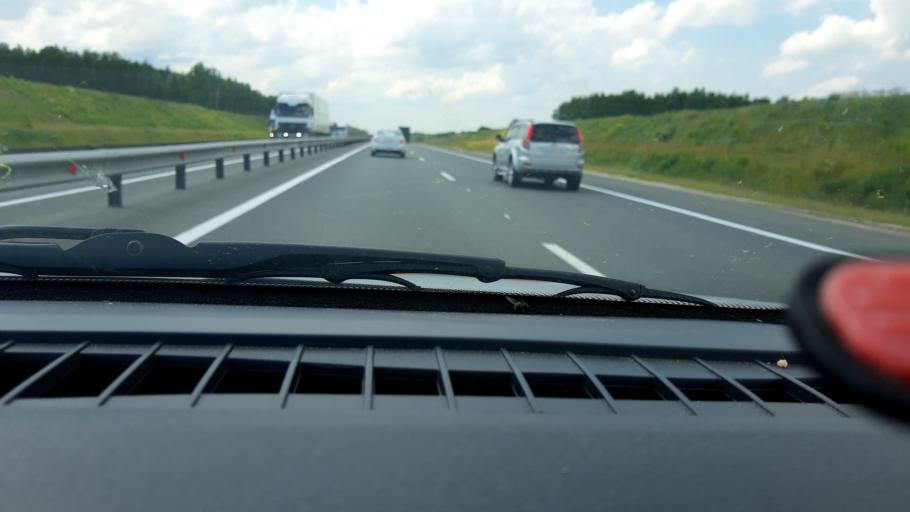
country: RU
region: Nizjnij Novgorod
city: Afonino
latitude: 56.1042
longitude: 44.0055
